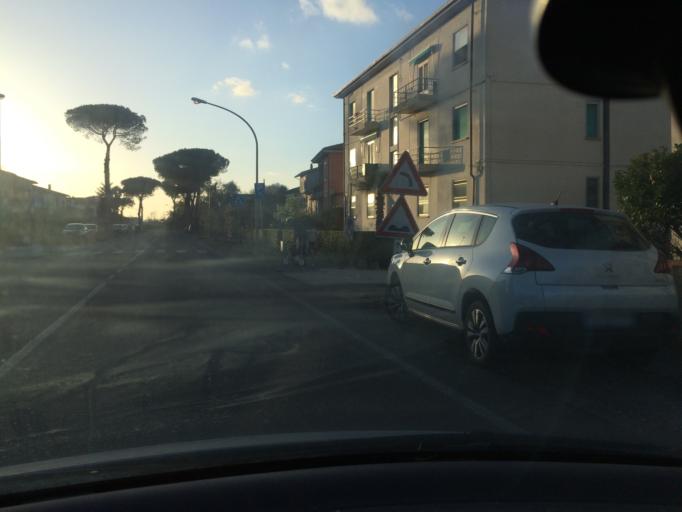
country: IT
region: Tuscany
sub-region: Province of Pisa
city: Gello
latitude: 43.7229
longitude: 10.4376
